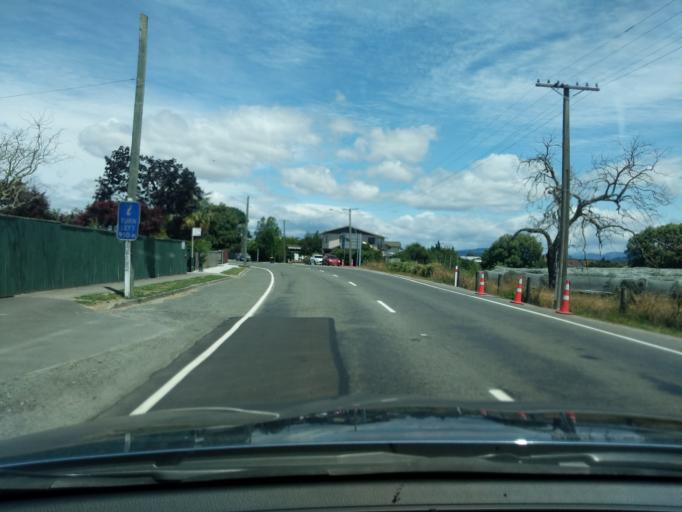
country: NZ
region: Tasman
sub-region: Tasman District
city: Motueka
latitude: -41.1024
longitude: 173.0119
